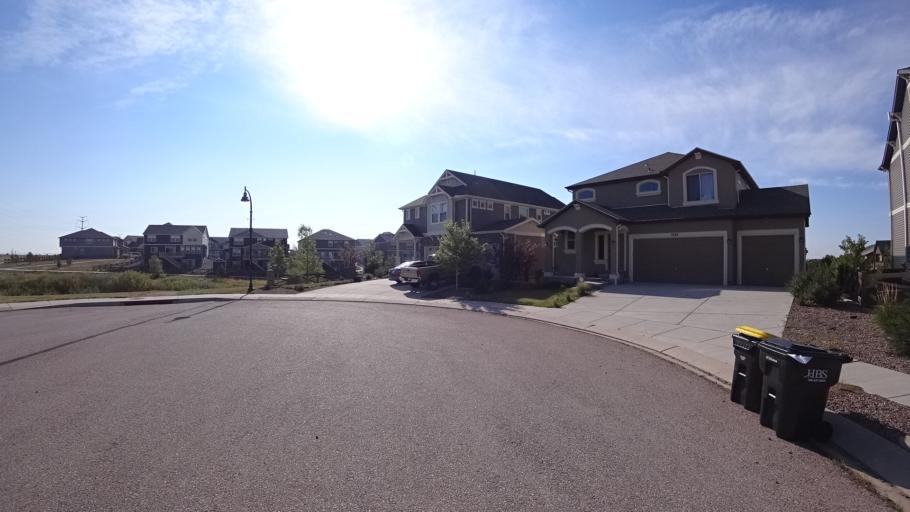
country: US
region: Colorado
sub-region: El Paso County
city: Black Forest
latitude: 38.9369
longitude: -104.6720
